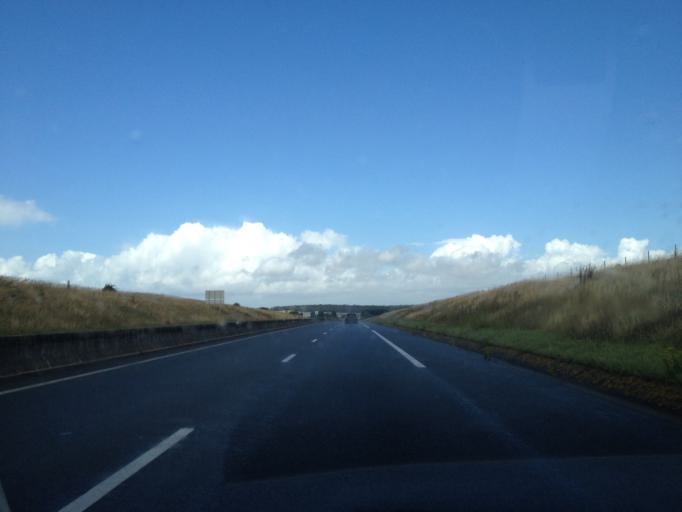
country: FR
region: Nord-Pas-de-Calais
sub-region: Departement du Pas-de-Calais
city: Saint-Josse
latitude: 50.4285
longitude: 1.6941
